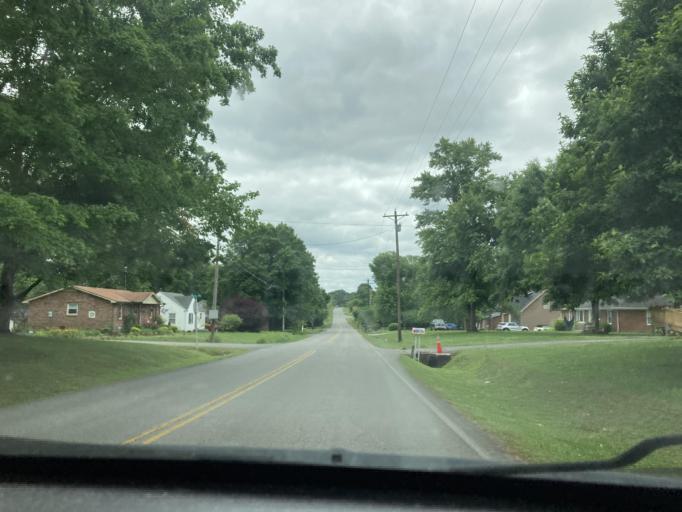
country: US
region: Tennessee
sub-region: Dickson County
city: Dickson
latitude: 36.0911
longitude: -87.3799
